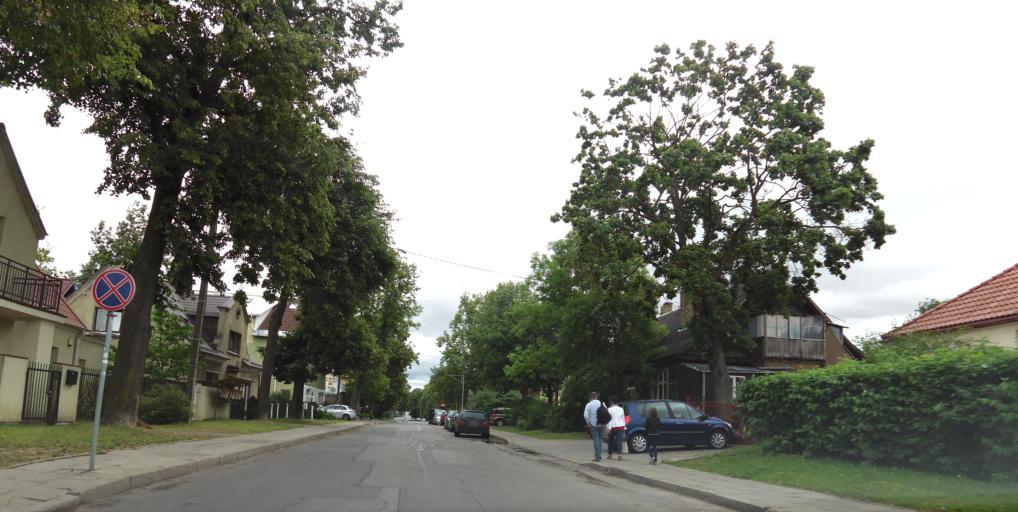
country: LT
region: Vilnius County
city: Seskine
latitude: 54.6949
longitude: 25.2488
